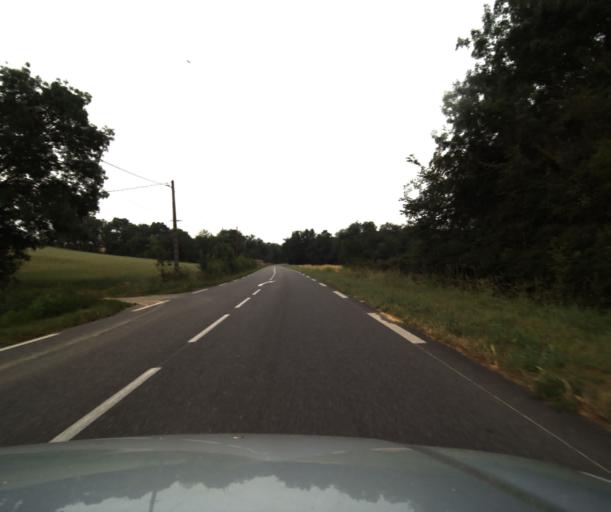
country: FR
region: Midi-Pyrenees
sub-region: Departement du Gers
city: Gimont
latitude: 43.7039
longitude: 0.8506
